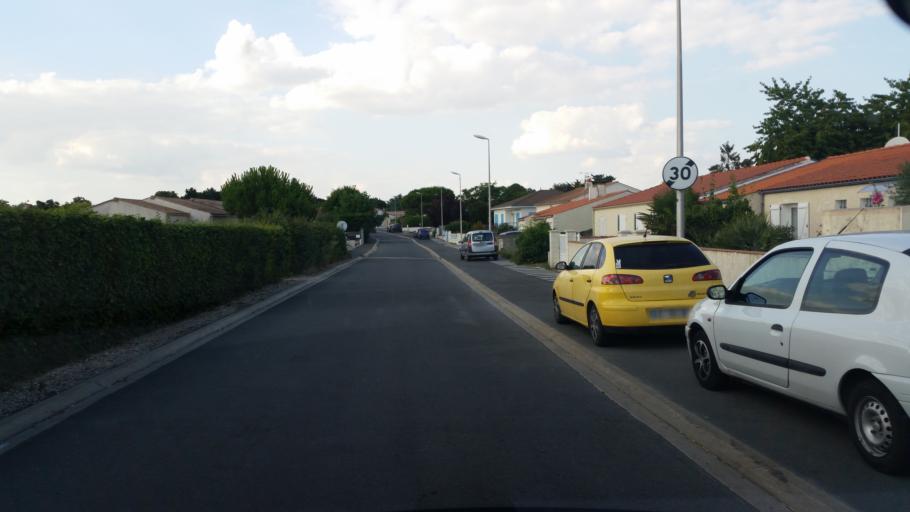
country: FR
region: Poitou-Charentes
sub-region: Departement de la Charente-Maritime
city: Andilly
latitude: 46.2518
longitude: -1.0248
